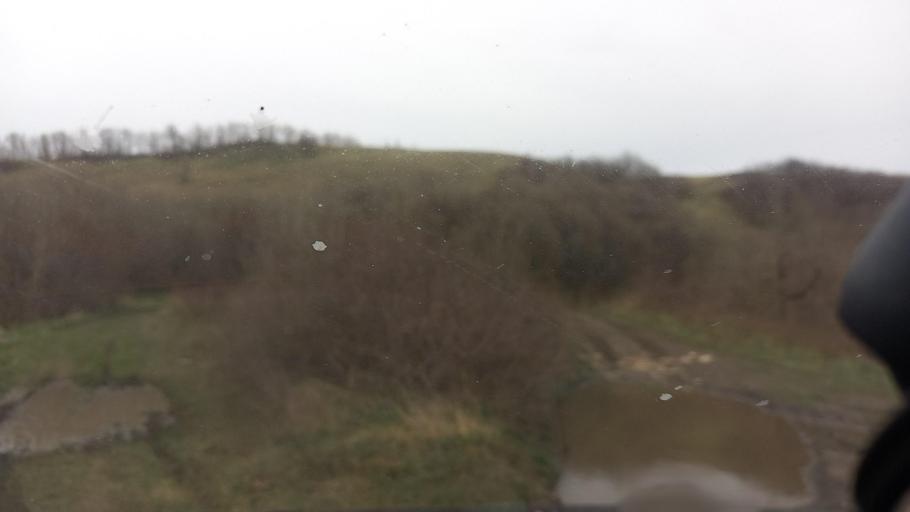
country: RU
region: Krasnodarskiy
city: Gelendzhik
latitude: 44.6150
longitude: 38.2104
